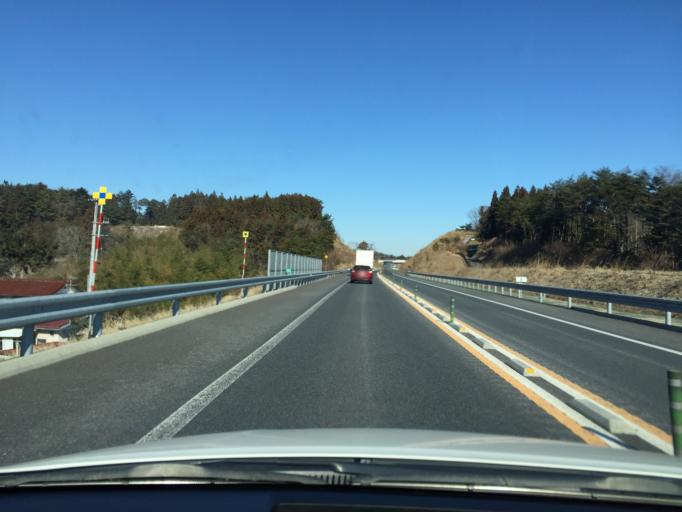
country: JP
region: Miyagi
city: Marumori
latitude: 37.7503
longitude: 140.9028
